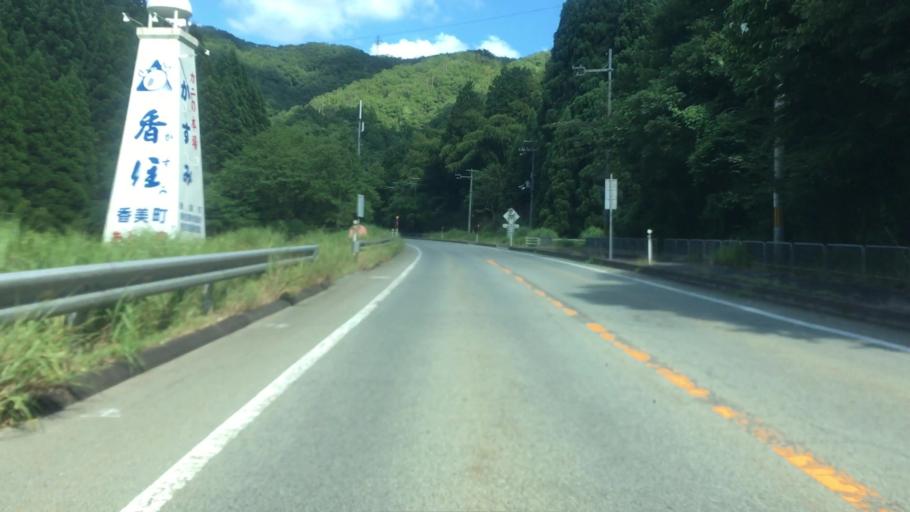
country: JP
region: Hyogo
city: Toyooka
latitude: 35.5772
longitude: 134.7534
